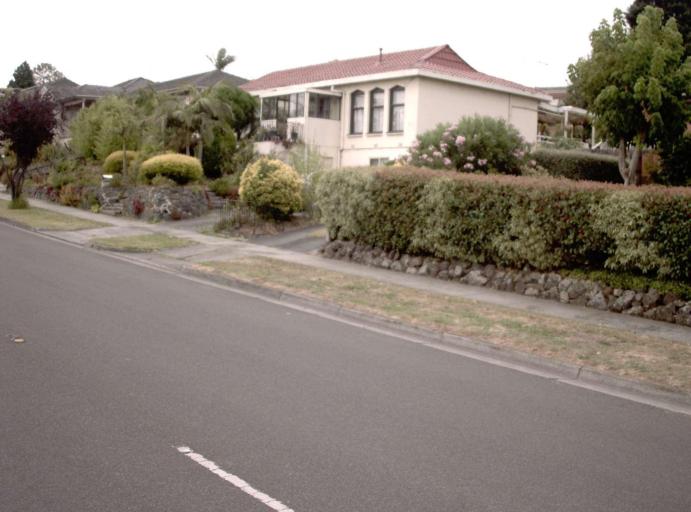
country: AU
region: Victoria
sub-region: Greater Dandenong
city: Dandenong North
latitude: -37.9556
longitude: 145.2251
